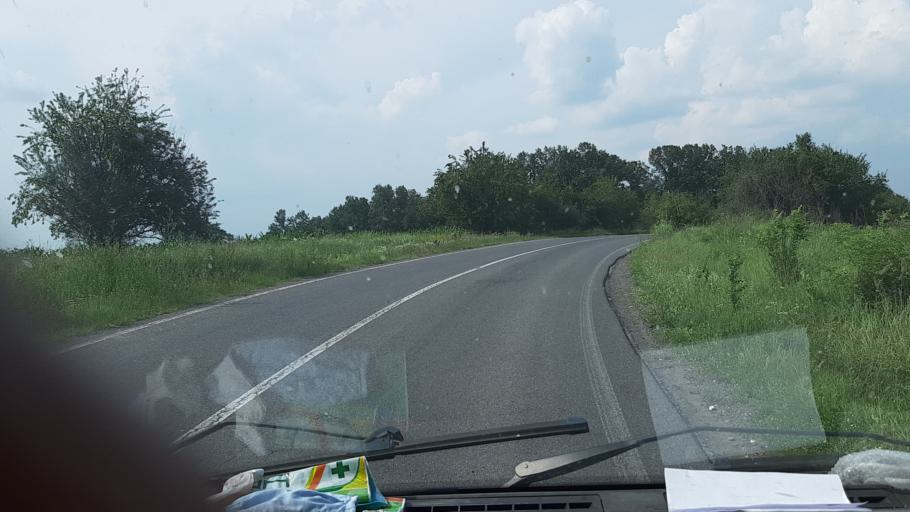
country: RO
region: Caras-Severin
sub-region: Comuna Farliug
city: Farliug
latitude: 45.5293
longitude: 21.8777
